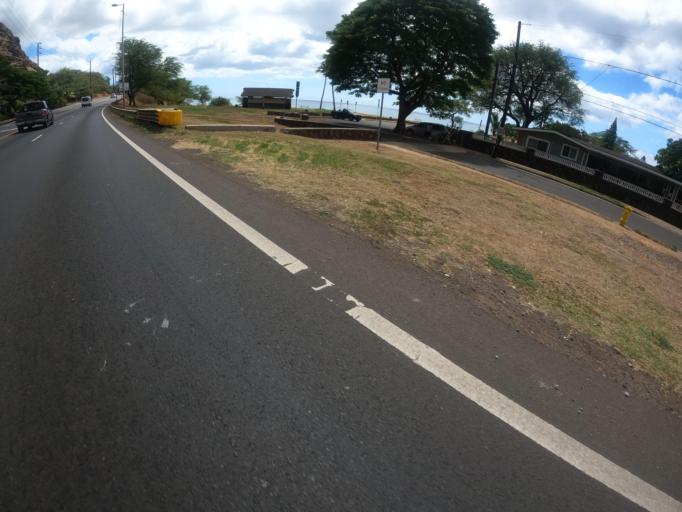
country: US
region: Hawaii
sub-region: Honolulu County
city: Nanakuli
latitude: 21.3698
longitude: -158.1358
